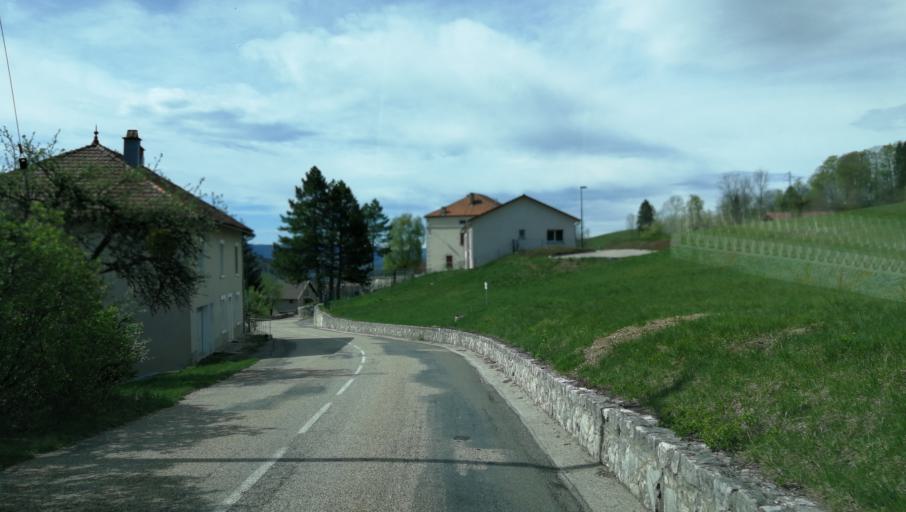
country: FR
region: Rhone-Alpes
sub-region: Departement de l'Ain
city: Arbent
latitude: 46.2538
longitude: 5.7784
